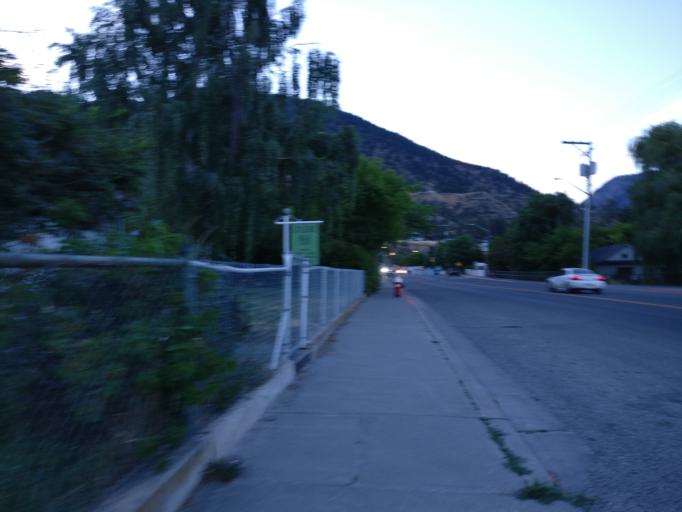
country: CA
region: British Columbia
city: Lillooet
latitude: 50.6894
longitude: -121.9373
